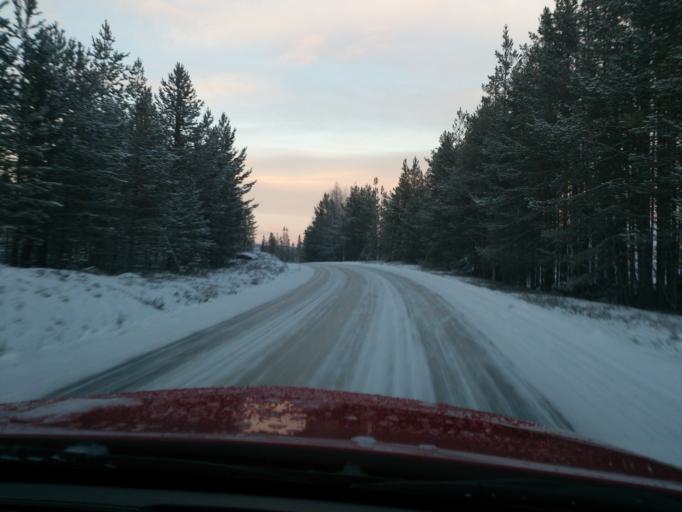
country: SE
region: Jaemtland
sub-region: Harjedalens Kommun
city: Sveg
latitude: 62.3972
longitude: 13.5233
